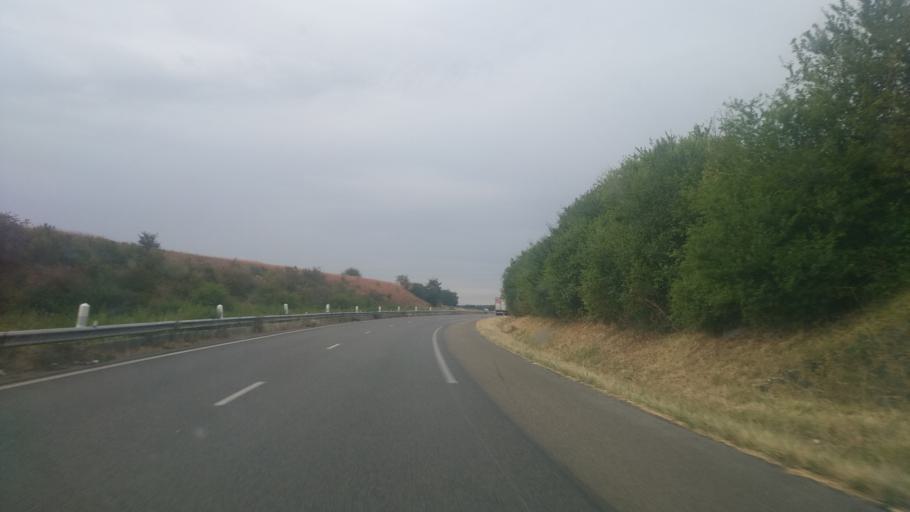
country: FR
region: Ile-de-France
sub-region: Departement de Seine-et-Marne
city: Vert-Saint-Denis
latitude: 48.5897
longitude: 2.6351
